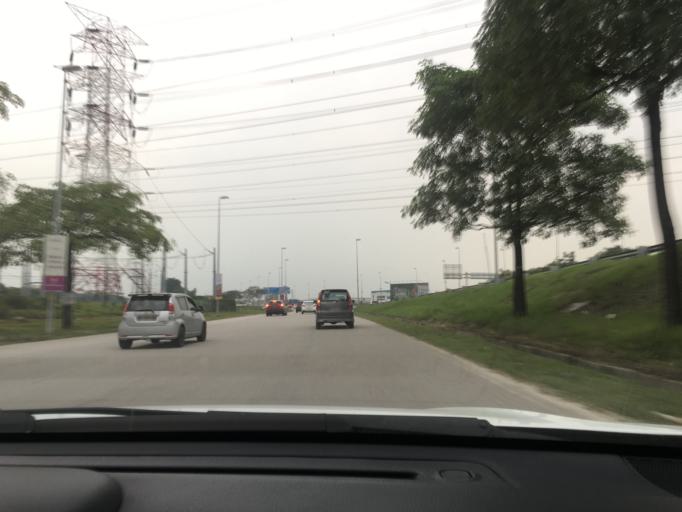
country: MY
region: Selangor
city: Klang
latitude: 3.1052
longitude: 101.4424
